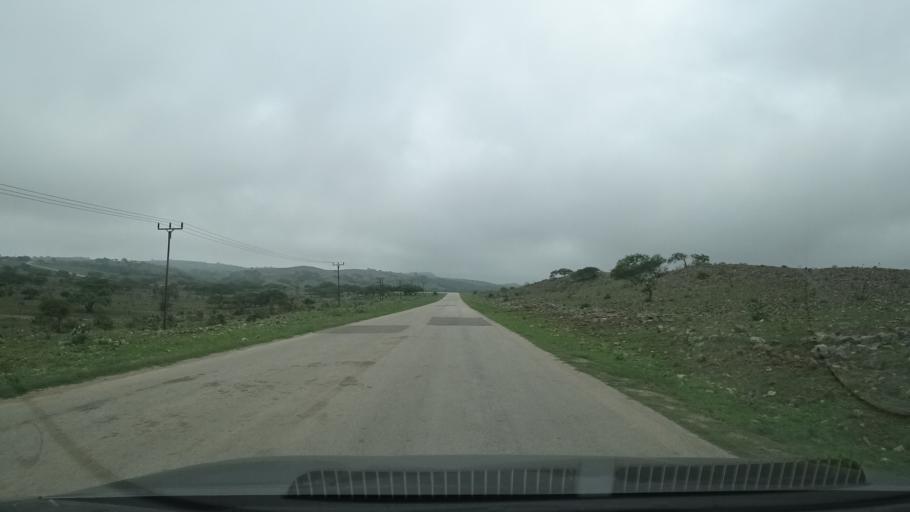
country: OM
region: Zufar
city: Salalah
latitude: 17.1187
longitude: 54.5698
